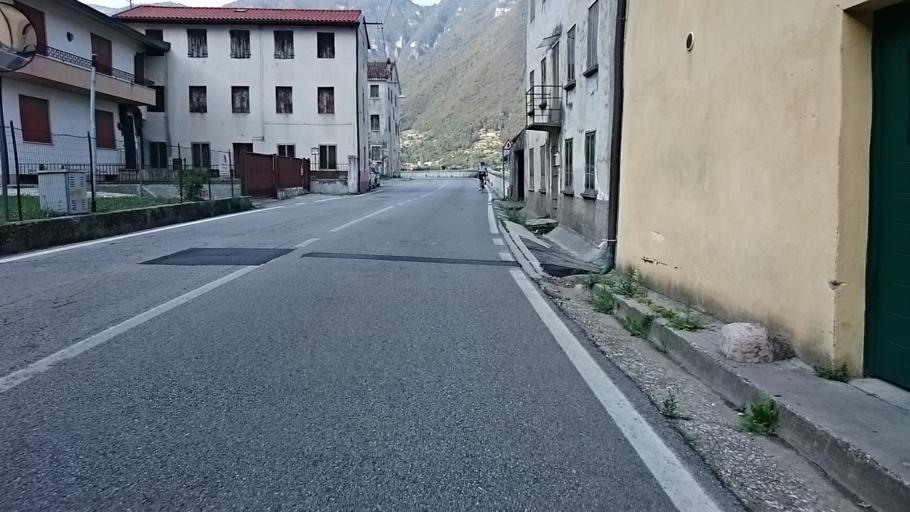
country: IT
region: Veneto
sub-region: Provincia di Vicenza
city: Campese
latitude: 45.8059
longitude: 11.7112
